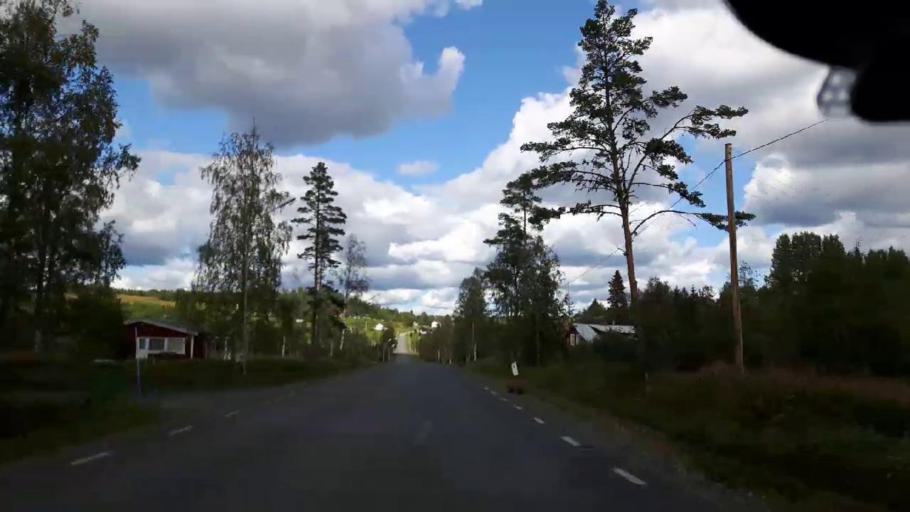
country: SE
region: Jaemtland
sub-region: Stroemsunds Kommun
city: Stroemsund
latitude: 63.2908
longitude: 15.5908
